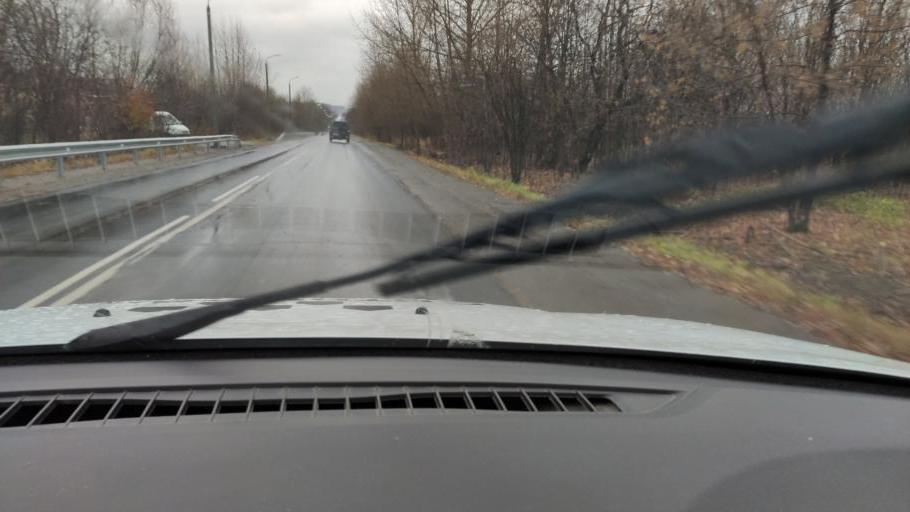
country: RU
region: Perm
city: Perm
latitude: 58.0382
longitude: 56.3862
